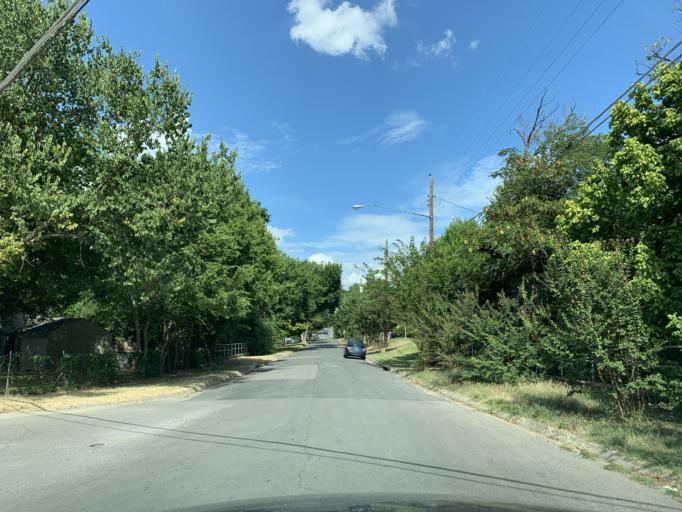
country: US
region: Texas
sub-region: Dallas County
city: Cockrell Hill
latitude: 32.7464
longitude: -96.8673
